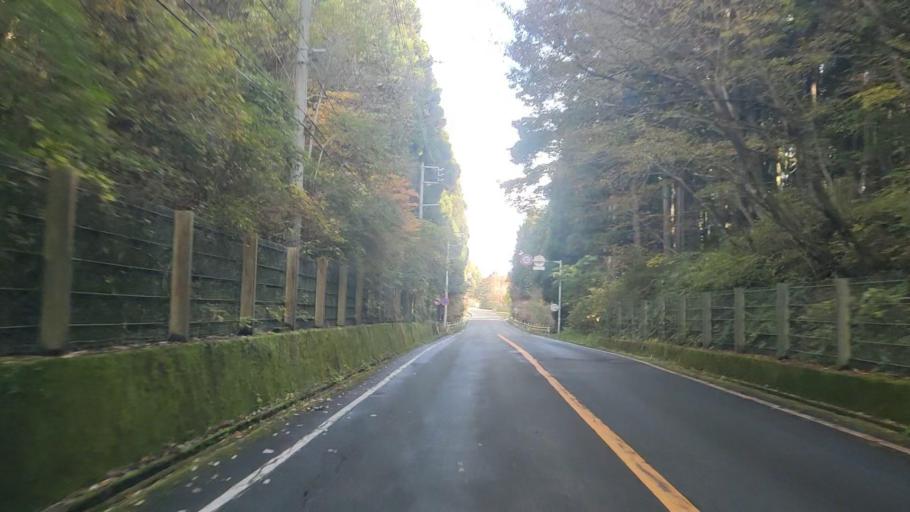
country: JP
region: Shizuoka
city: Fujinomiya
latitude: 35.2962
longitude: 138.6660
